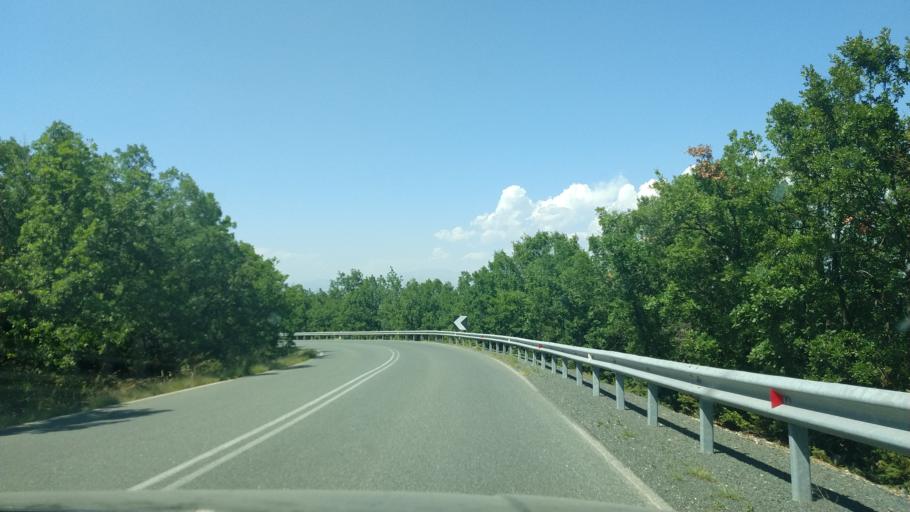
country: GR
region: West Macedonia
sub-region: Nomos Grevenon
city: Grevena
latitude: 40.0239
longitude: 21.4850
